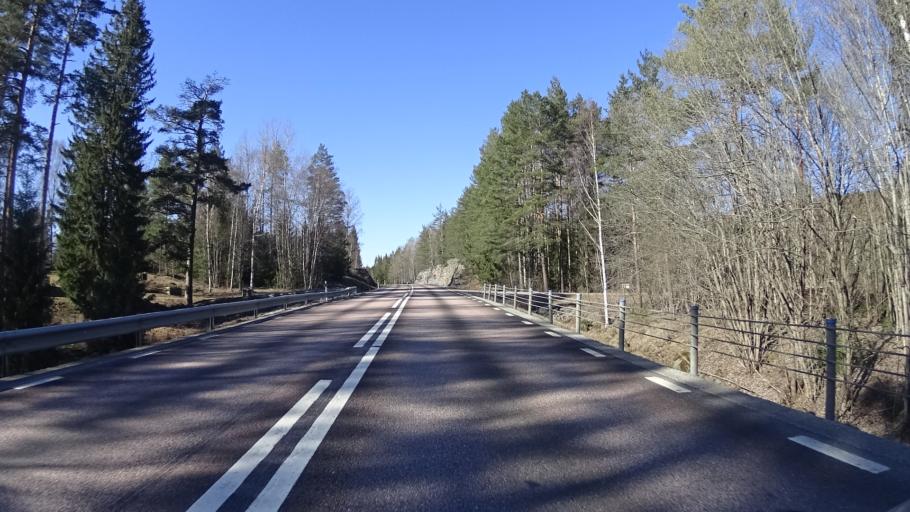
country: SE
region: Vaermland
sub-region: Karlstads Kommun
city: Edsvalla
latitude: 59.6102
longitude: 12.9886
